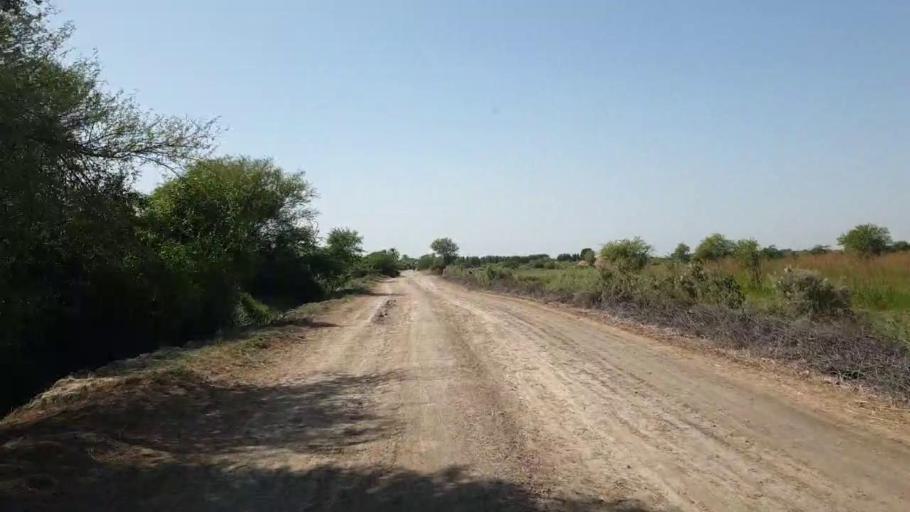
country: PK
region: Sindh
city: Tando Bago
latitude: 24.7049
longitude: 69.0301
